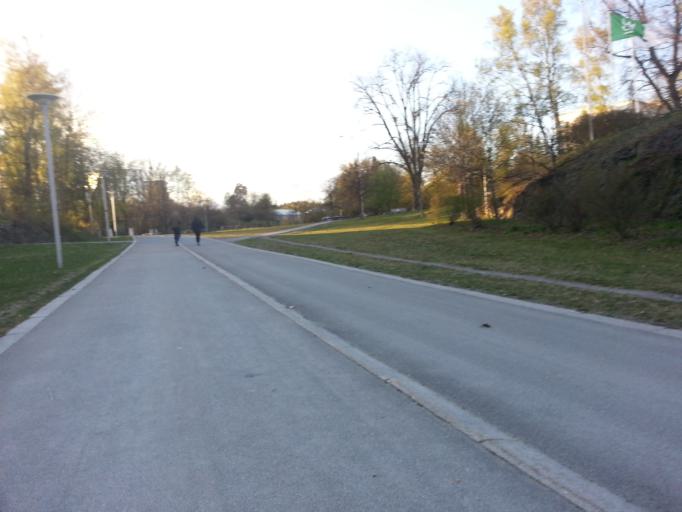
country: NO
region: Akershus
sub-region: Baerum
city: Lysaker
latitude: 59.9022
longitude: 10.6311
